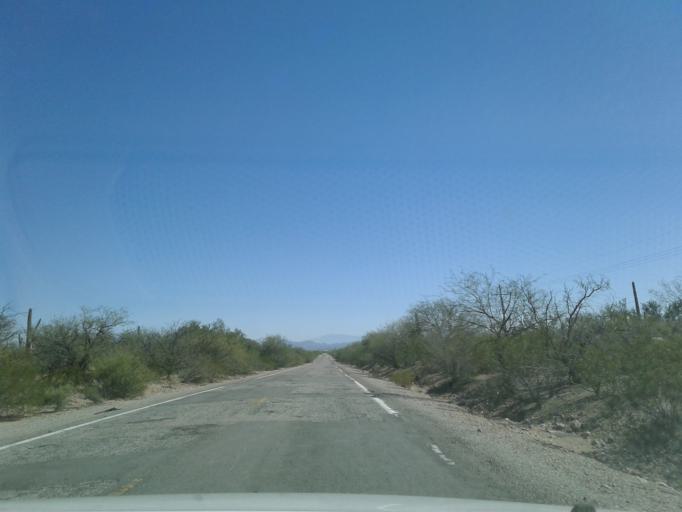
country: US
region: Arizona
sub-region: Pima County
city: Avra Valley
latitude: 32.3758
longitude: -111.4693
